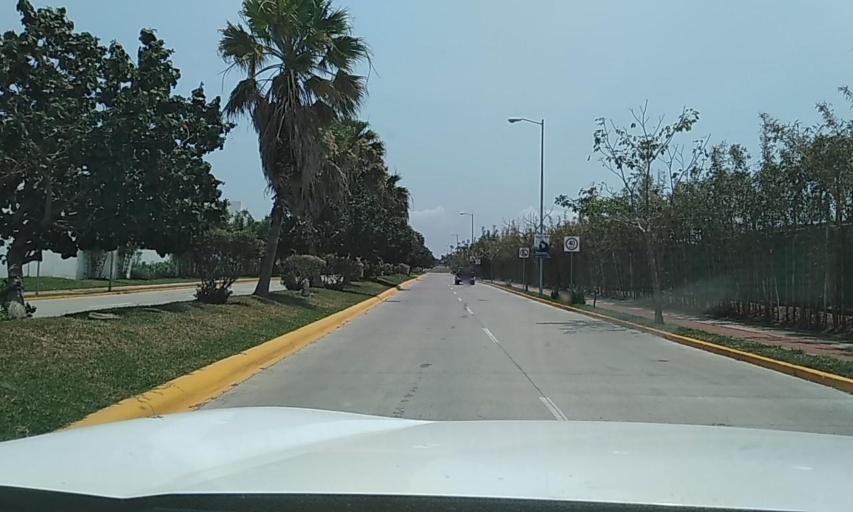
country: MX
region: Veracruz
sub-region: Veracruz
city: Hacienda Sotavento
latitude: 19.1287
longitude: -96.1723
